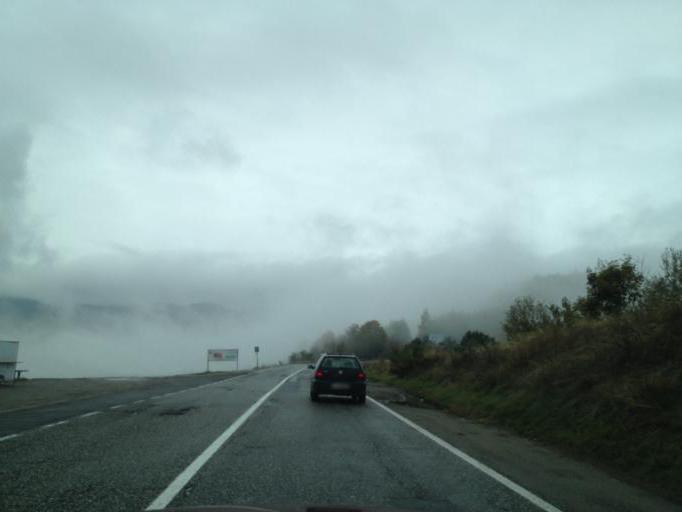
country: RO
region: Brasov
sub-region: Municipiul Brasov
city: Moeciu de Jos
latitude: 45.4860
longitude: 25.3153
